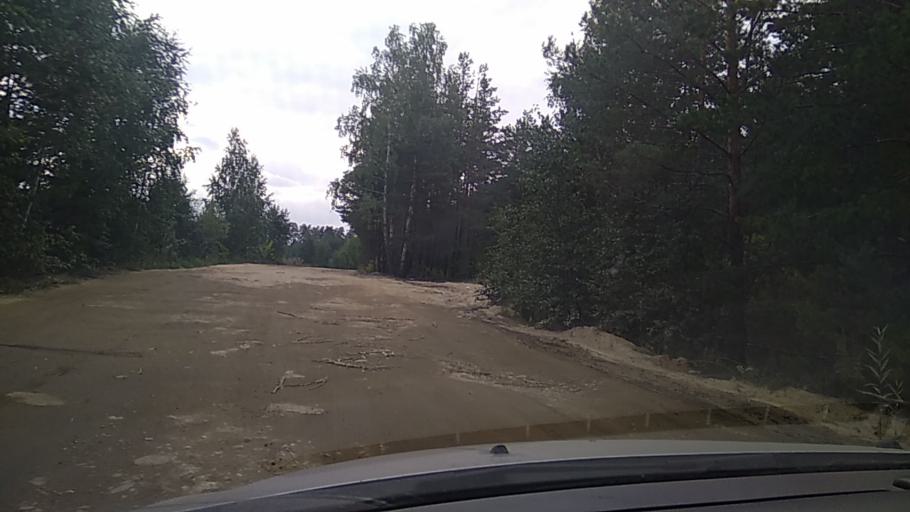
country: RU
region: Chelyabinsk
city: Kyshtym
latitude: 55.6810
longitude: 60.5732
